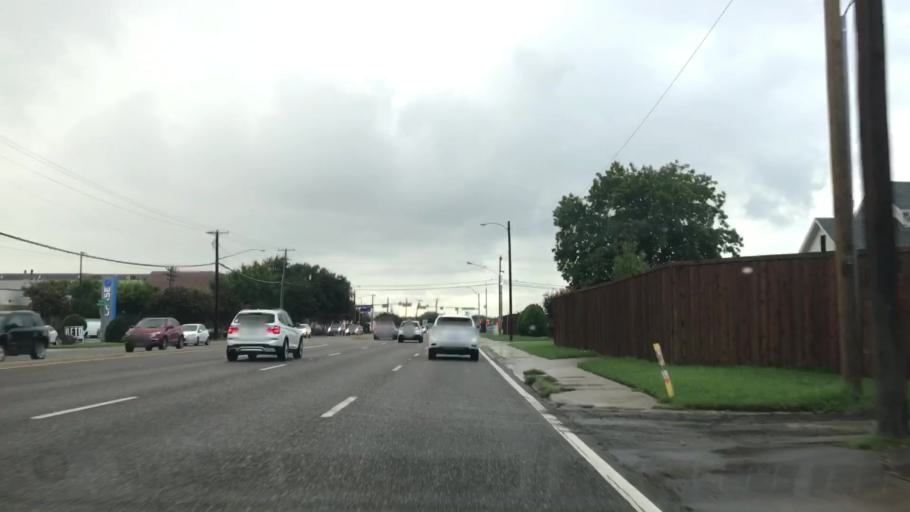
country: US
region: Texas
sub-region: Dallas County
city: University Park
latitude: 32.9059
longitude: -96.8040
